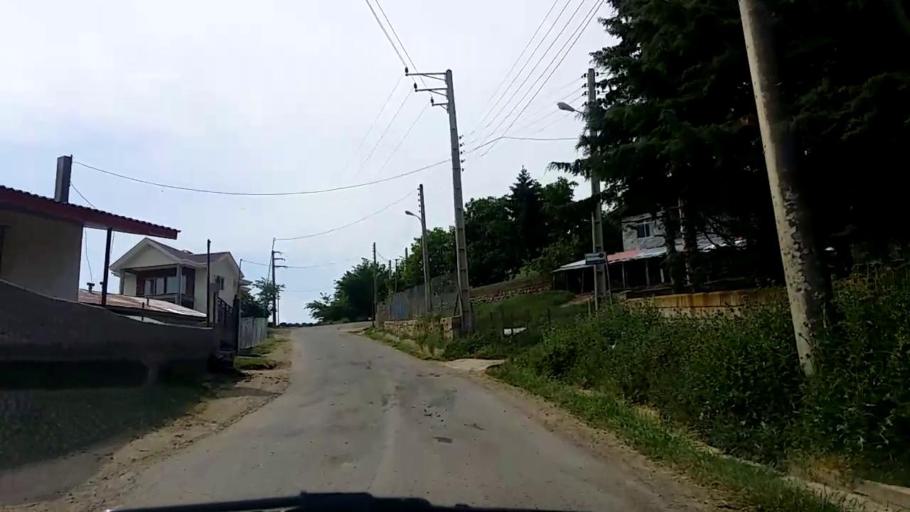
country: IR
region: Mazandaran
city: `Abbasabad
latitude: 36.5514
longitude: 51.1831
